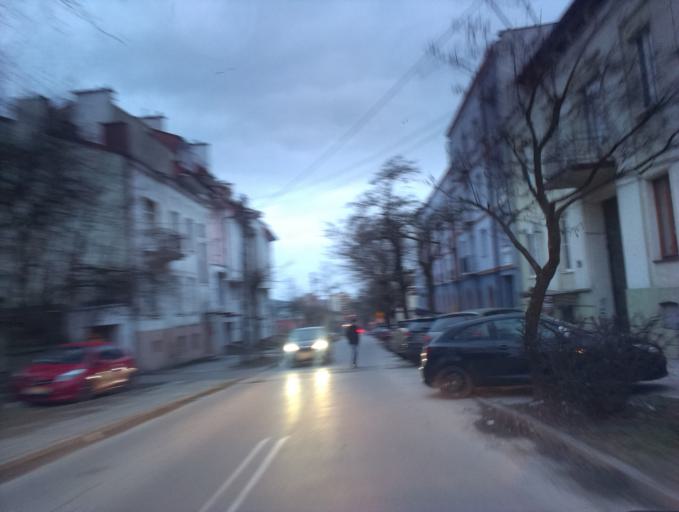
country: PL
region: Swietokrzyskie
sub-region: Powiat kielecki
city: Kielce
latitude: 50.8630
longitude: 20.6342
